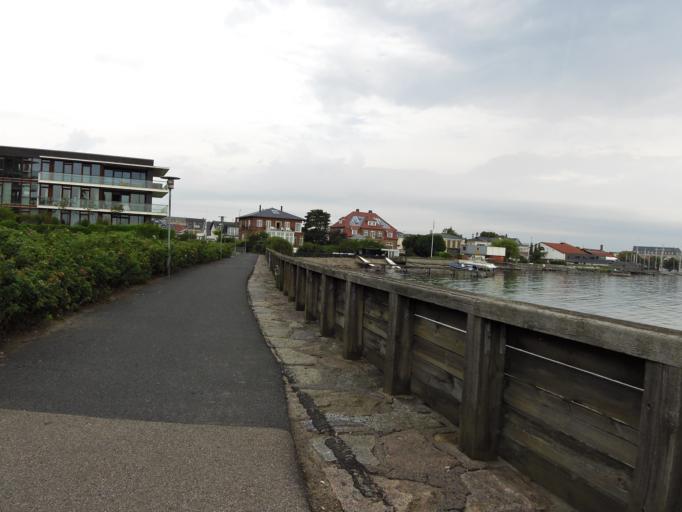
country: DK
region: Capital Region
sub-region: Gentofte Kommune
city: Charlottenlund
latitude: 55.7287
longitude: 12.5832
